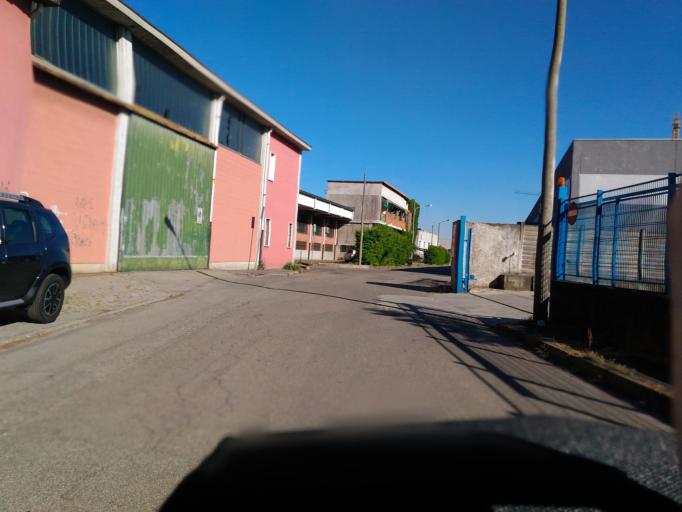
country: IT
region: Lombardy
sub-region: Citta metropolitana di Milano
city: Poasco-Sorigherio
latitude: 45.3982
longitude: 9.2481
